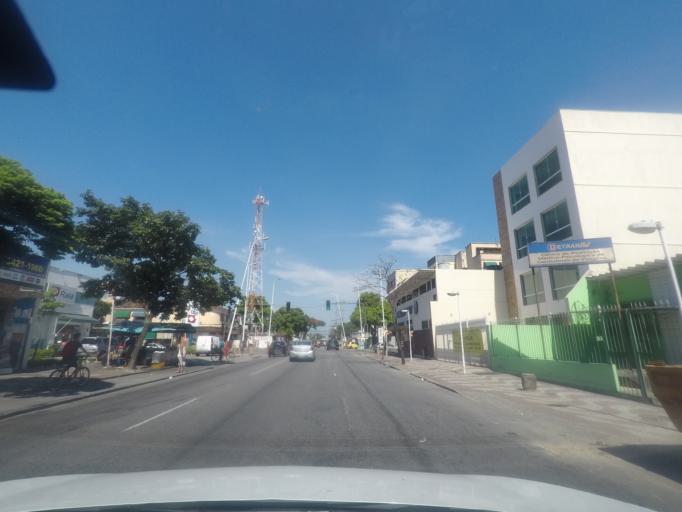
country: BR
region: Rio de Janeiro
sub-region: Nilopolis
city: Nilopolis
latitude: -22.8796
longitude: -43.4628
